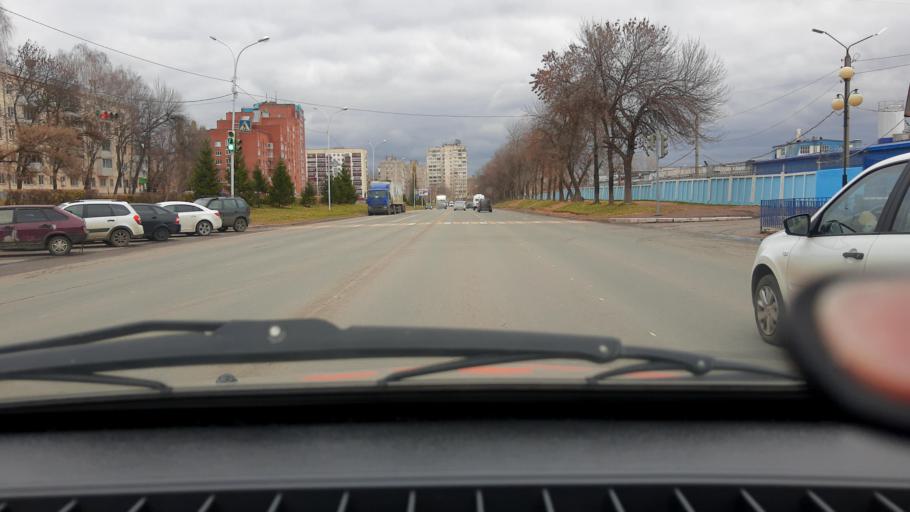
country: RU
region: Bashkortostan
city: Ufa
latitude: 54.8054
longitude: 56.1056
